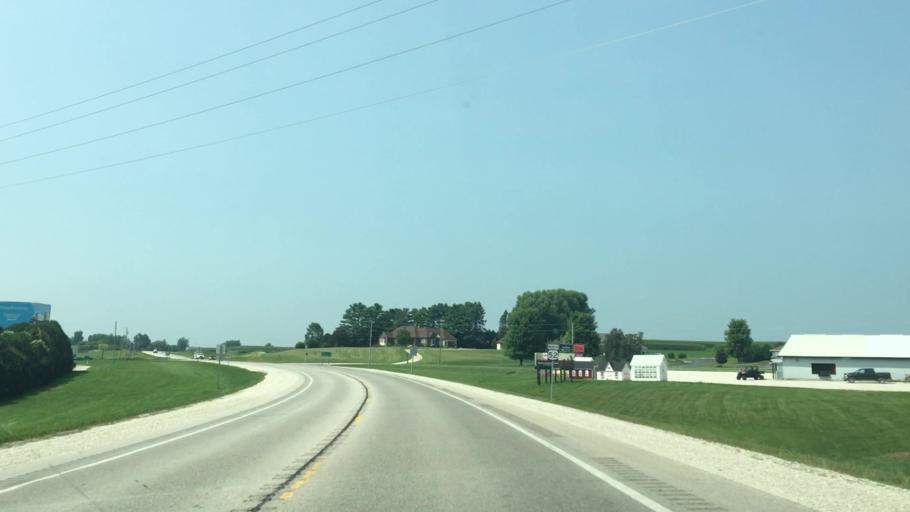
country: US
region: Iowa
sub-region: Winneshiek County
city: Decorah
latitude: 43.1890
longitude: -91.8649
